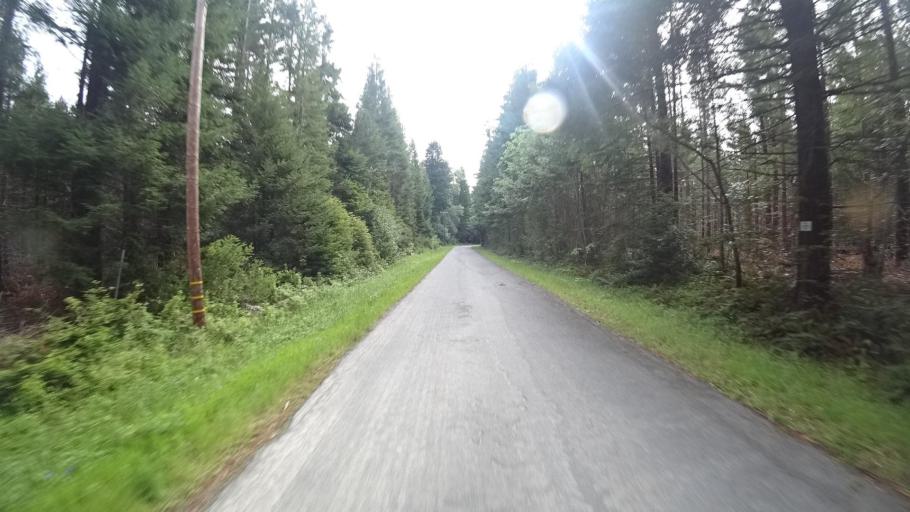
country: US
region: California
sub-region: Humboldt County
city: Redway
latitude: 40.3439
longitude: -123.8867
